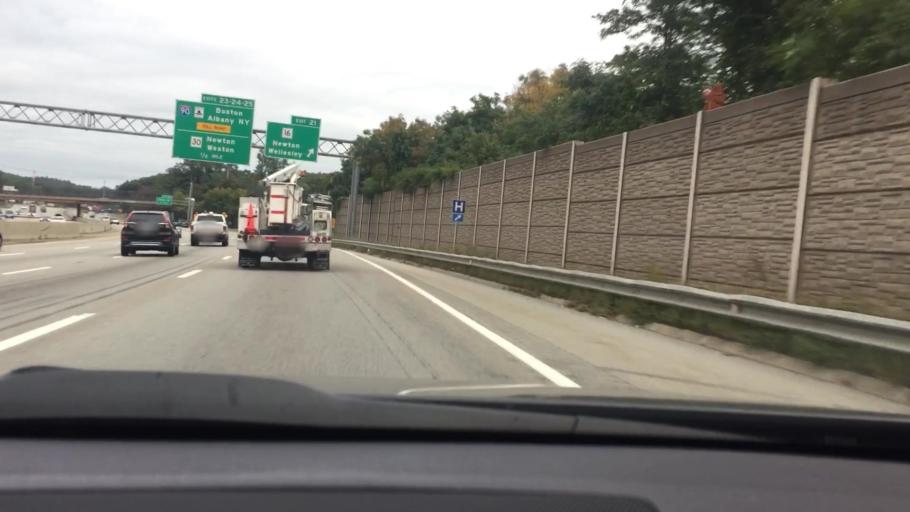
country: US
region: Massachusetts
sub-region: Middlesex County
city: Newton
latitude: 42.3261
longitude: -71.2500
